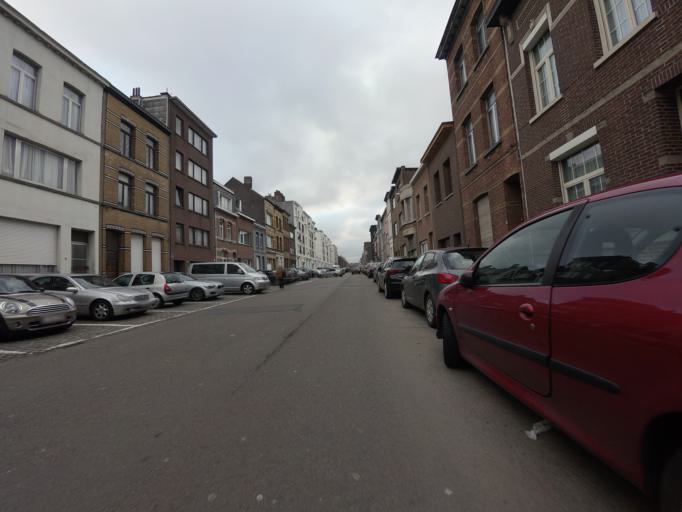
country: BE
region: Flanders
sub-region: Provincie Antwerpen
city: Hoboken
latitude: 51.1851
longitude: 4.3772
